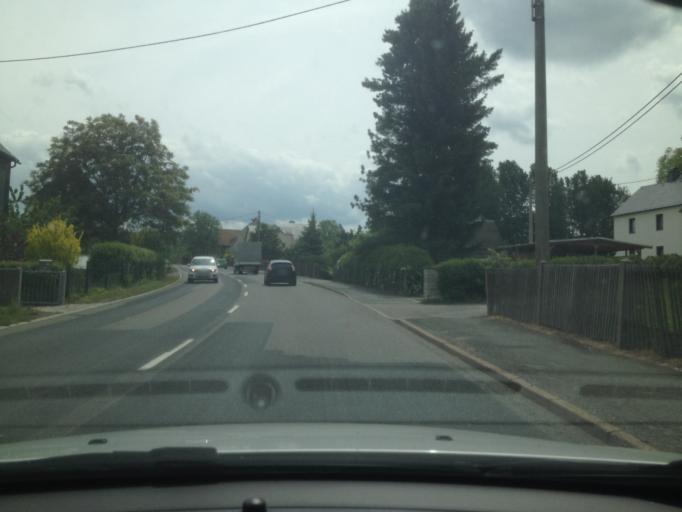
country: DE
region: Saxony
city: Stollberg
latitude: 50.6813
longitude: 12.7629
